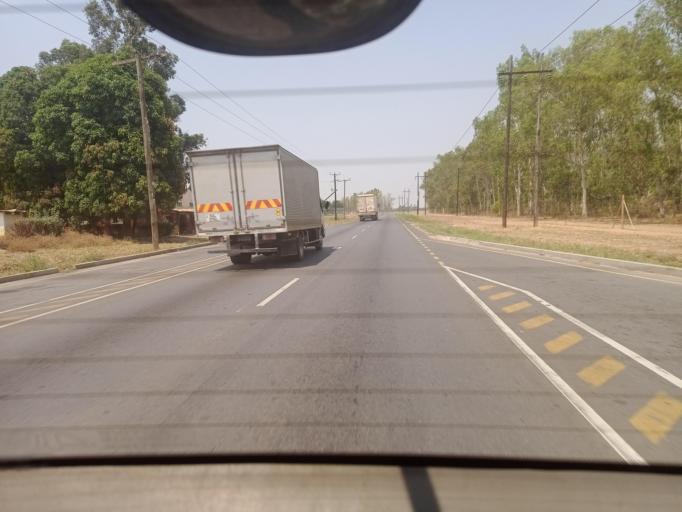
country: ZM
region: Lusaka
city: Lusaka
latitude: -15.2879
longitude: 28.3779
